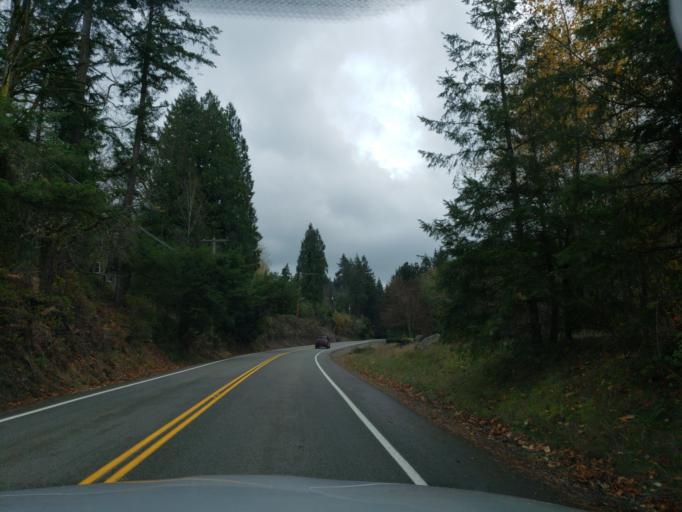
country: US
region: Washington
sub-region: King County
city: Woodinville
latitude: 47.7509
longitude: -122.1330
